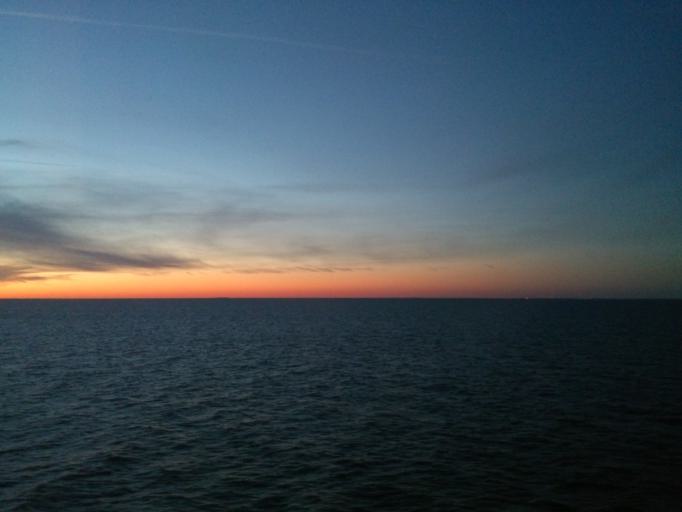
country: FI
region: Uusimaa
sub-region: Raaseporin
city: Hanko
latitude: 59.5890
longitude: 22.7243
